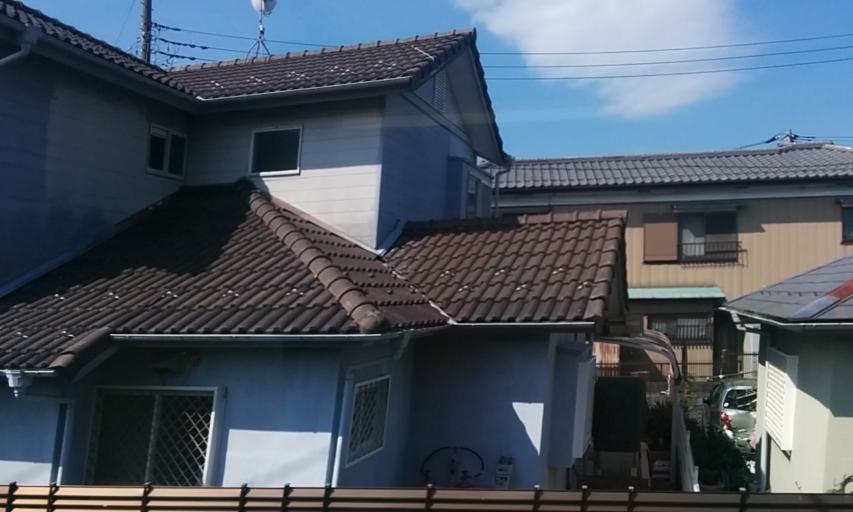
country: JP
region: Saitama
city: Kazo
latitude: 36.1255
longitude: 139.5915
